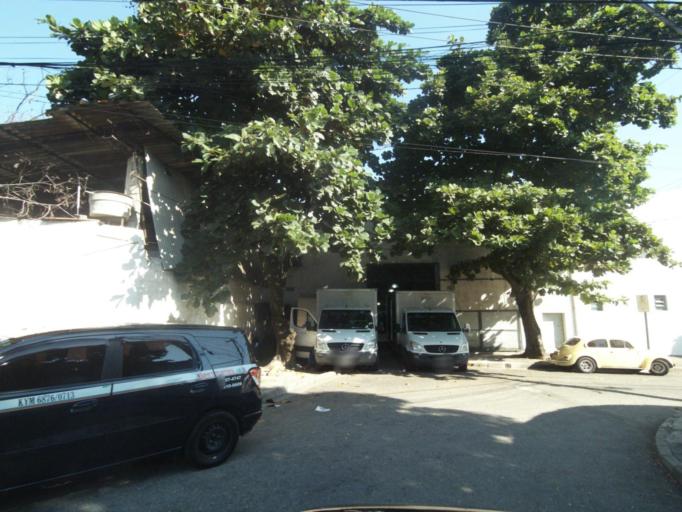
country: BR
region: Rio de Janeiro
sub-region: Niteroi
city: Niteroi
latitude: -22.8868
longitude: -43.1176
